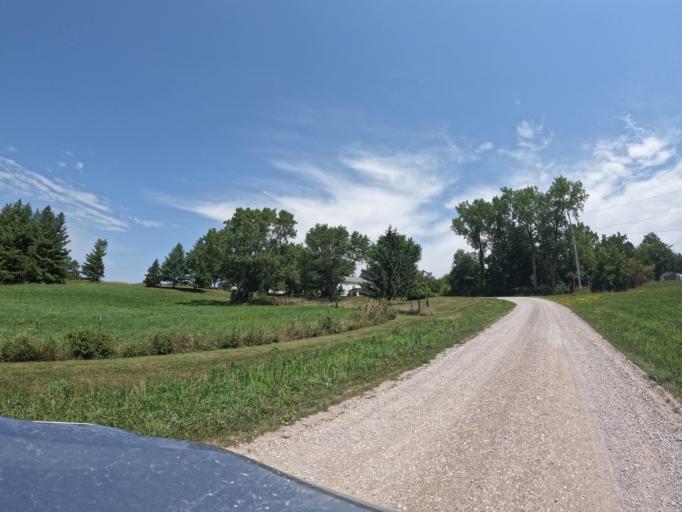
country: US
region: Iowa
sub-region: Appanoose County
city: Centerville
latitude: 40.7793
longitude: -92.9500
